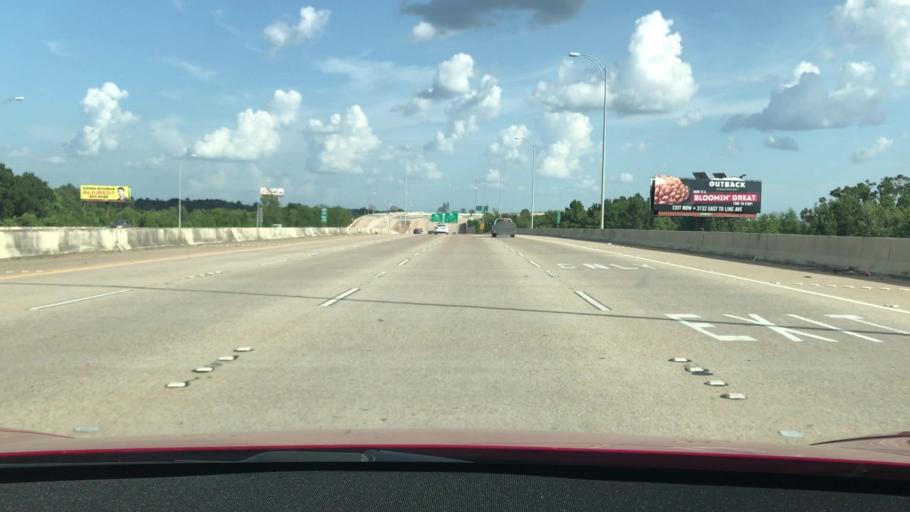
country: US
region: Louisiana
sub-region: Bossier Parish
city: Bossier City
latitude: 32.4288
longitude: -93.7531
